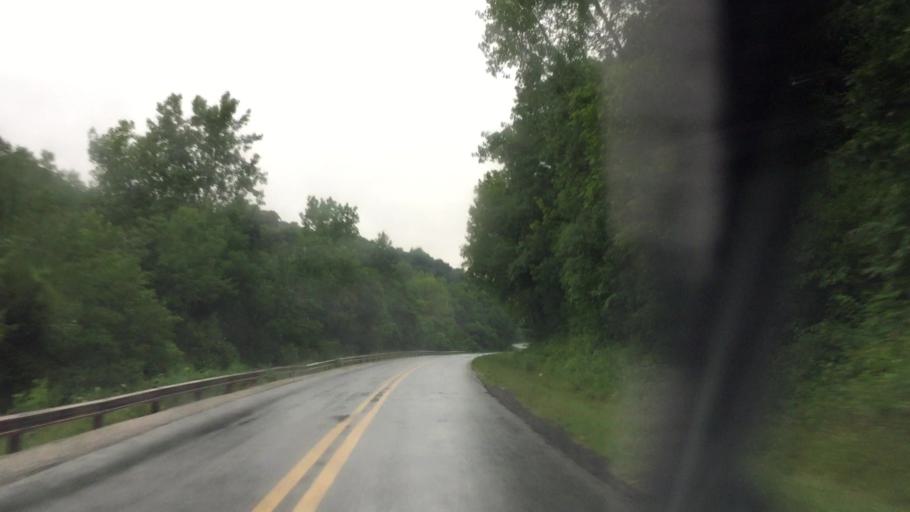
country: US
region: Iowa
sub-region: Lee County
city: Fort Madison
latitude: 40.6069
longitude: -91.2787
